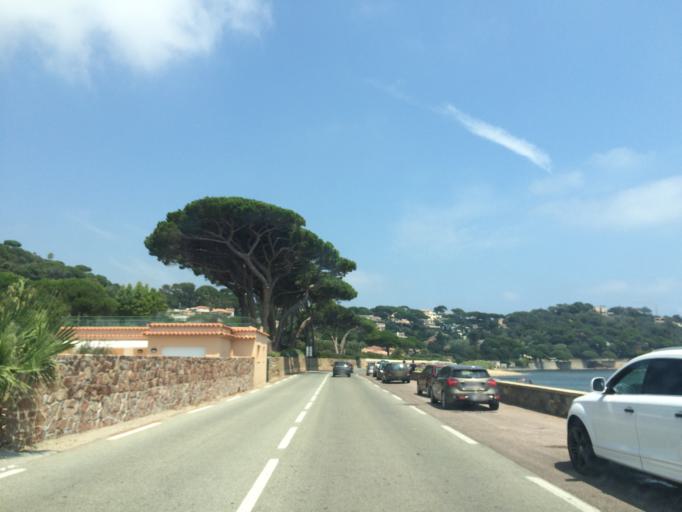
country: FR
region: Provence-Alpes-Cote d'Azur
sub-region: Departement du Var
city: Sainte-Maxime
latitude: 43.3119
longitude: 6.6548
